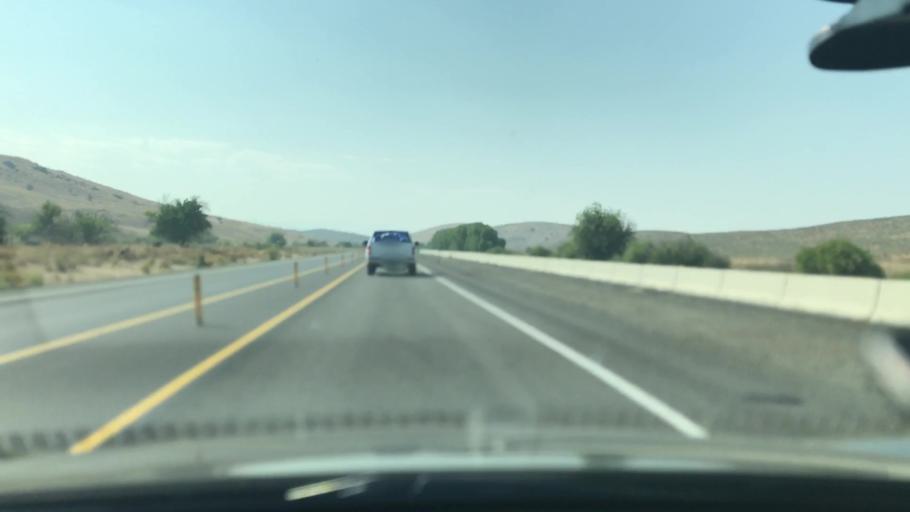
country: US
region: Oregon
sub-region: Baker County
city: Baker City
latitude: 44.6749
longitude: -117.6379
